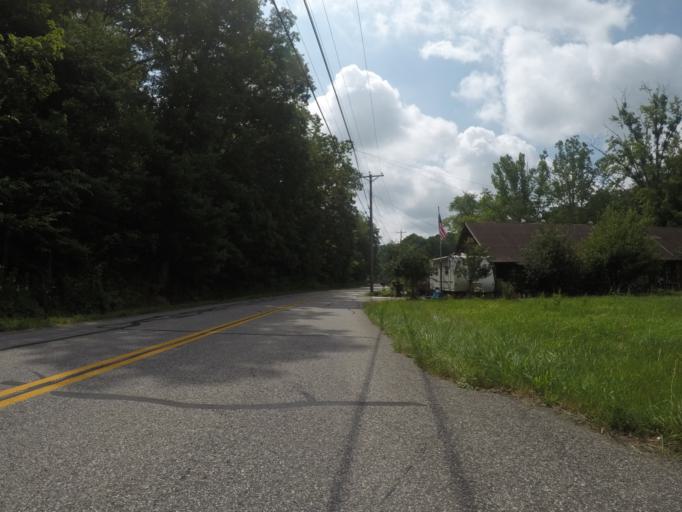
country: US
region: Kentucky
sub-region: Boyd County
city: Meads
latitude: 38.4166
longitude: -82.6902
